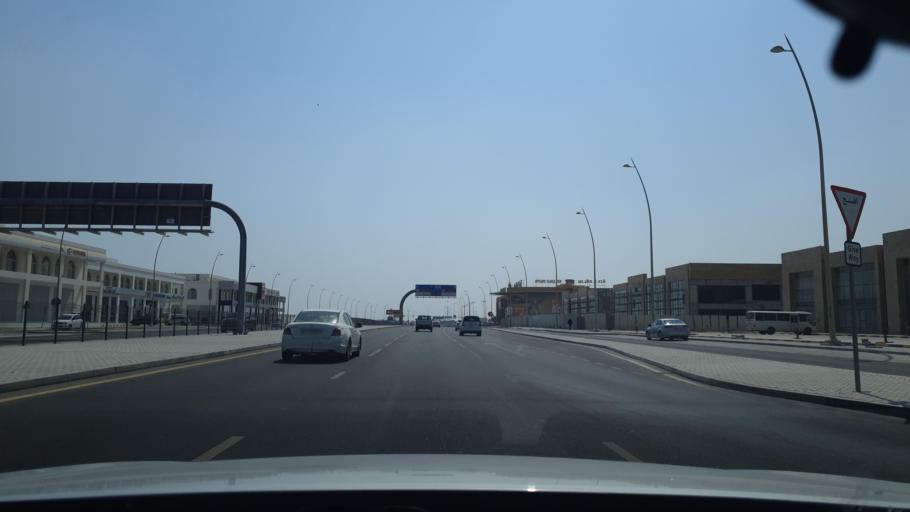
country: QA
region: Al Khawr
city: Al Khawr
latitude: 25.6690
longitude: 51.5008
